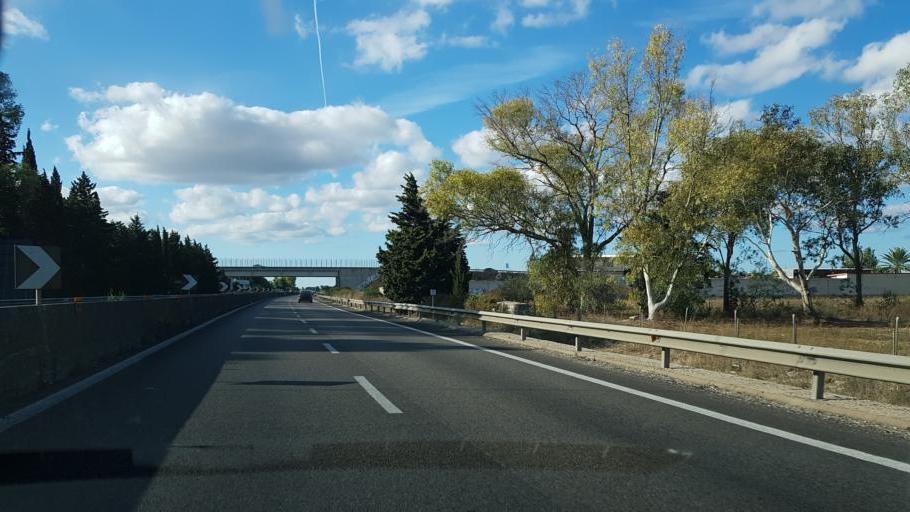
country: IT
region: Apulia
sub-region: Provincia di Lecce
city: Giorgilorio
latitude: 40.3774
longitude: 18.1382
